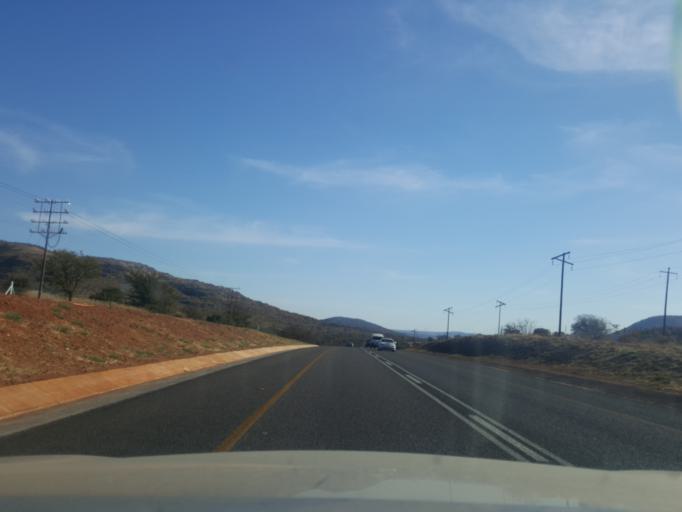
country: ZA
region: North-West
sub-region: Ngaka Modiri Molema District Municipality
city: Zeerust
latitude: -25.5270
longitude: 26.1506
